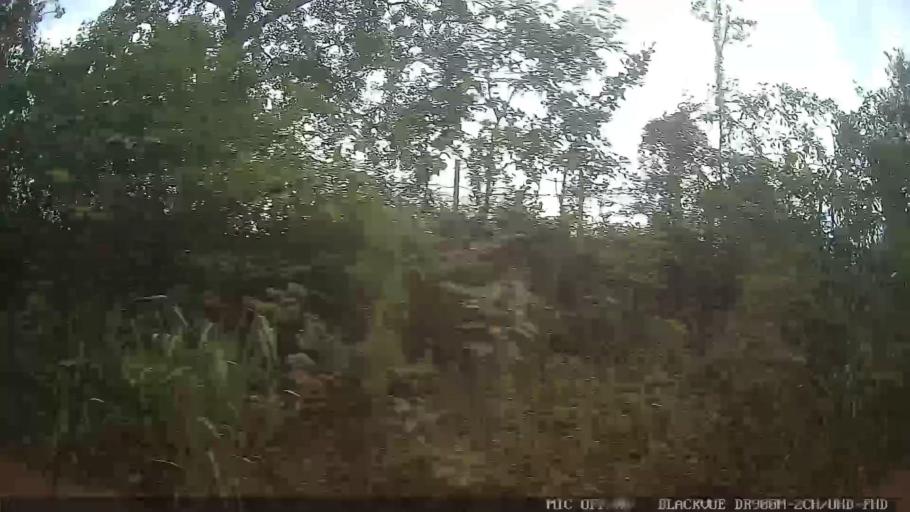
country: BR
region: Sao Paulo
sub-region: Bom Jesus Dos Perdoes
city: Bom Jesus dos Perdoes
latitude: -23.1347
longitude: -46.5076
